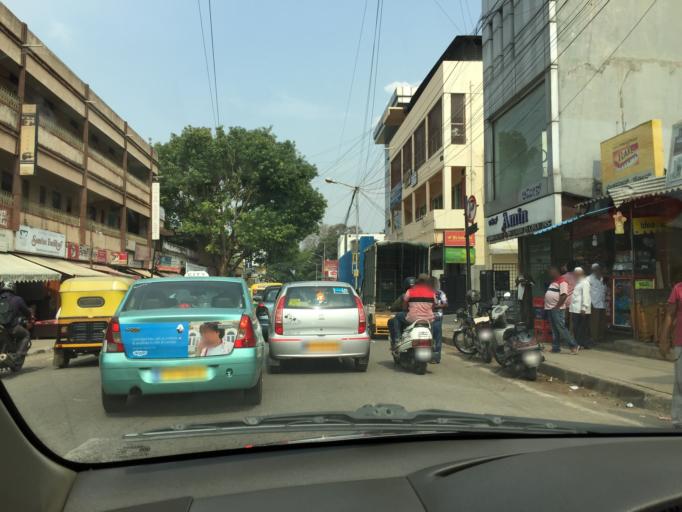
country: IN
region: Karnataka
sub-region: Bangalore Urban
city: Bangalore
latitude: 12.9807
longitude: 77.6029
